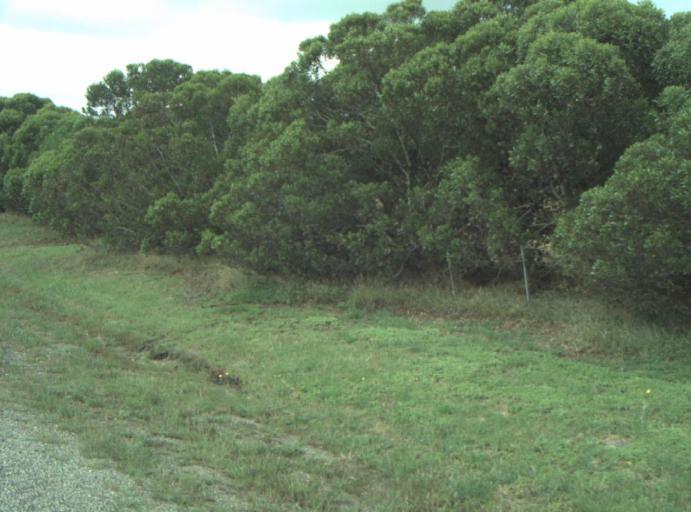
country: AU
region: Victoria
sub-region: Greater Geelong
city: Lara
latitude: -37.8747
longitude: 144.3225
